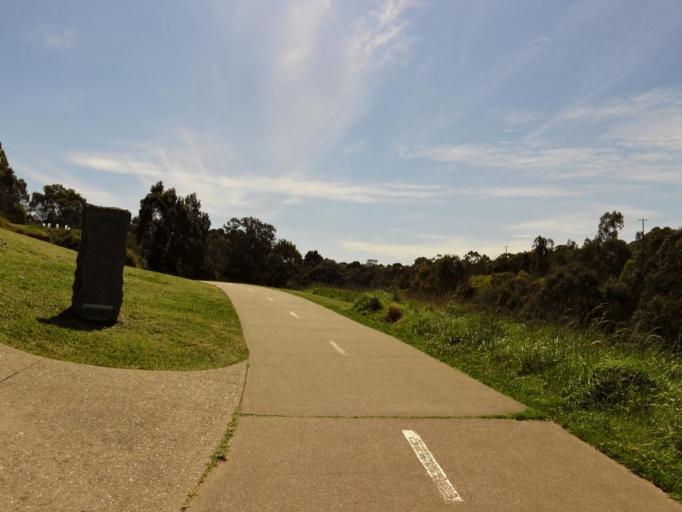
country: AU
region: Victoria
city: Abbotsford
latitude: -37.7917
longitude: 145.0051
